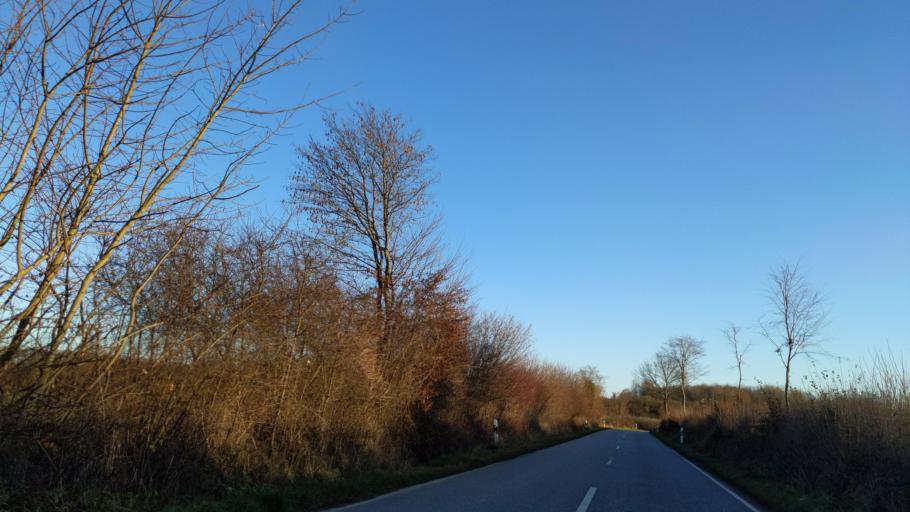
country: DE
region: Schleswig-Holstein
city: Travemuende
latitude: 53.9706
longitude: 10.8430
